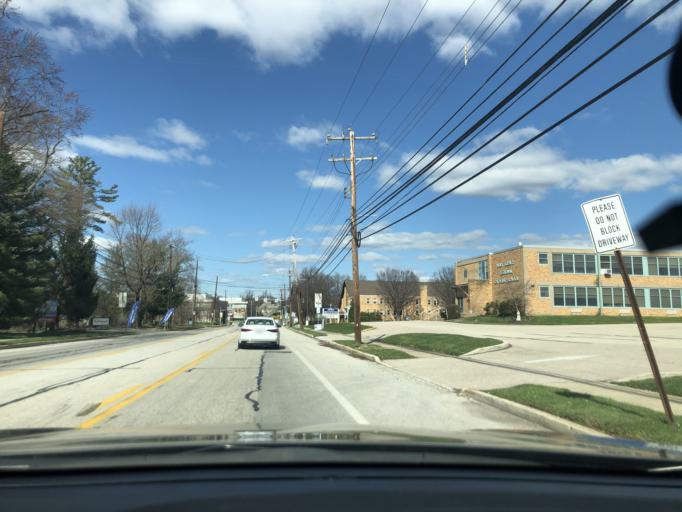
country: US
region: Pennsylvania
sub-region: Montgomery County
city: Blue Bell
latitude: 40.1304
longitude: -75.2799
